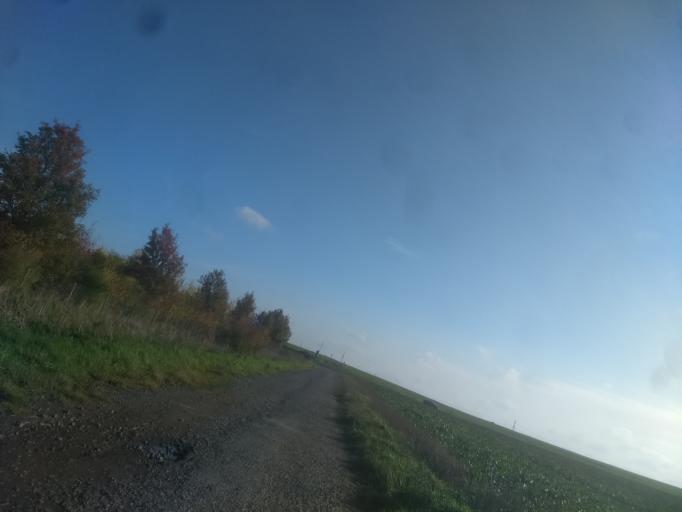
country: FR
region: Nord-Pas-de-Calais
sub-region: Departement du Pas-de-Calais
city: Tilloy-les-Mofflaines
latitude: 50.2729
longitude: 2.8072
